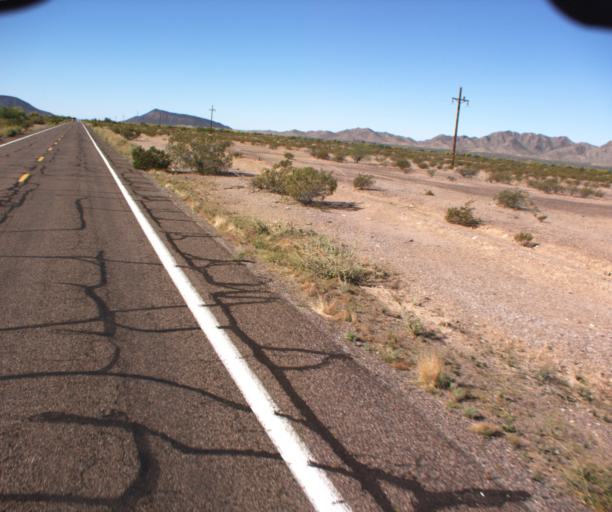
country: US
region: Arizona
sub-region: Maricopa County
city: Gila Bend
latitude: 32.8163
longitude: -112.7905
